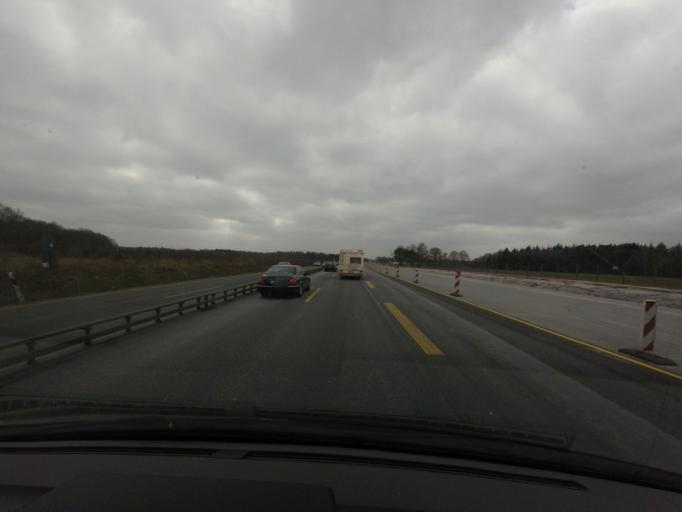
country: DE
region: Schleswig-Holstein
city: Bonningstedt
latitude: 53.6742
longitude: 9.9423
